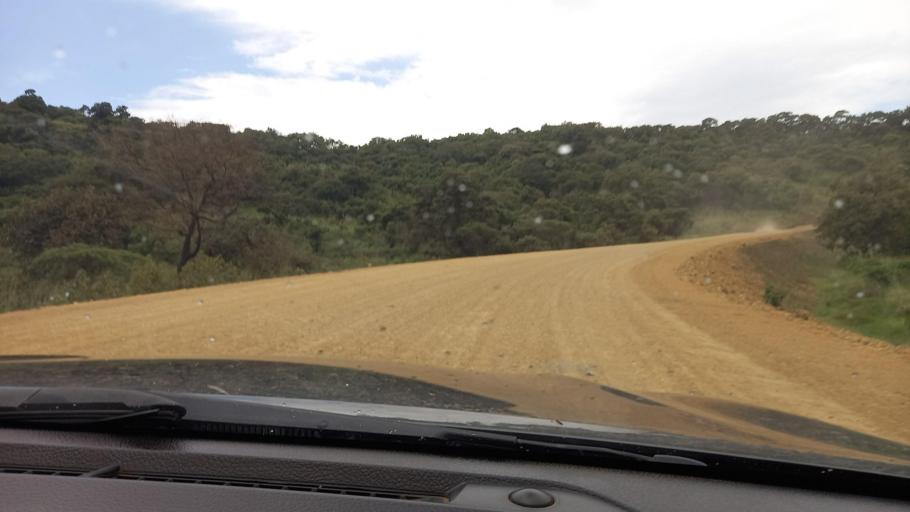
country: ET
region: Southern Nations, Nationalities, and People's Region
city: Mizan Teferi
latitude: 6.1997
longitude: 35.6726
